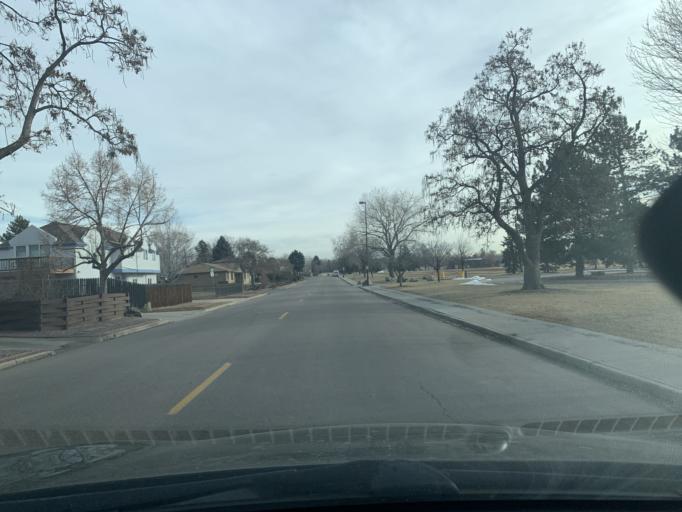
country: US
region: Colorado
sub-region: Jefferson County
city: Edgewater
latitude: 39.7530
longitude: -105.0519
